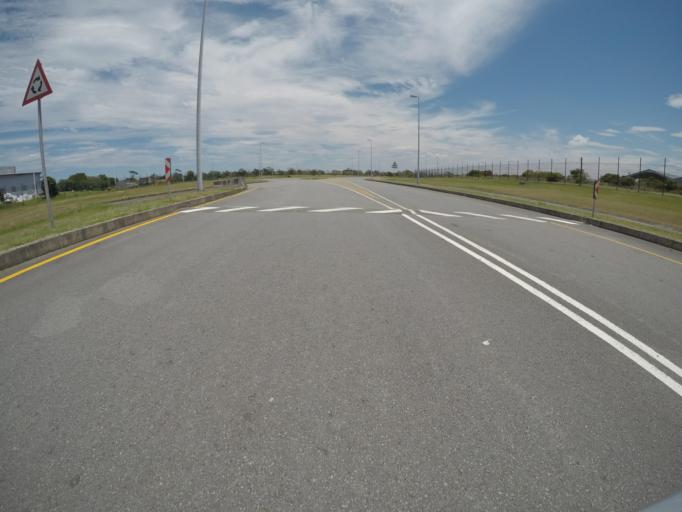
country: ZA
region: Eastern Cape
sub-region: Buffalo City Metropolitan Municipality
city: East London
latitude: -33.0569
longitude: 27.8358
